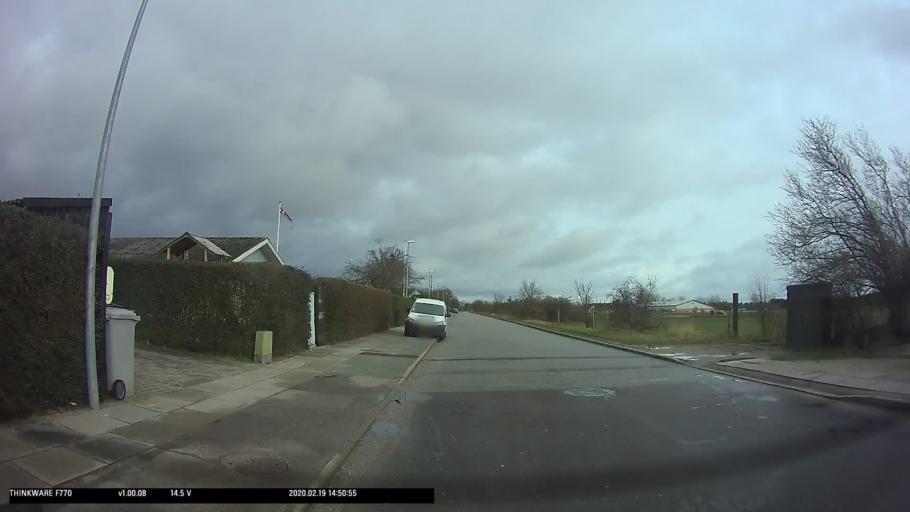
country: DK
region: Capital Region
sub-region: Tarnby Kommune
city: Tarnby
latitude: 55.5904
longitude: 12.5765
